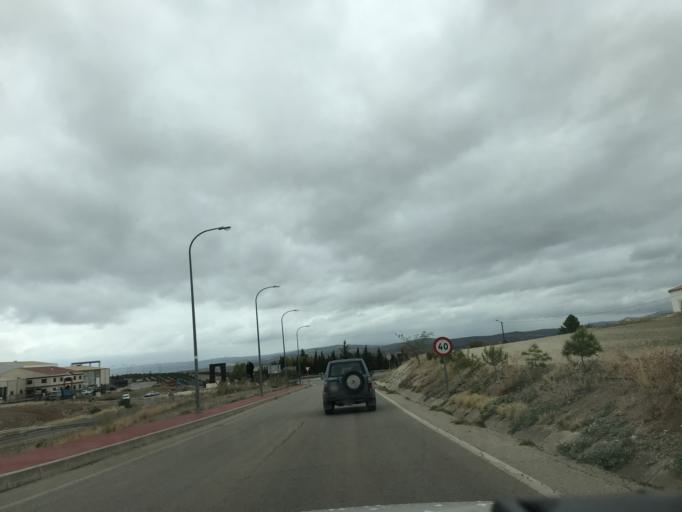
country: ES
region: Andalusia
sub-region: Provincia de Jaen
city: Peal de Becerro
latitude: 37.9171
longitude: -3.1316
